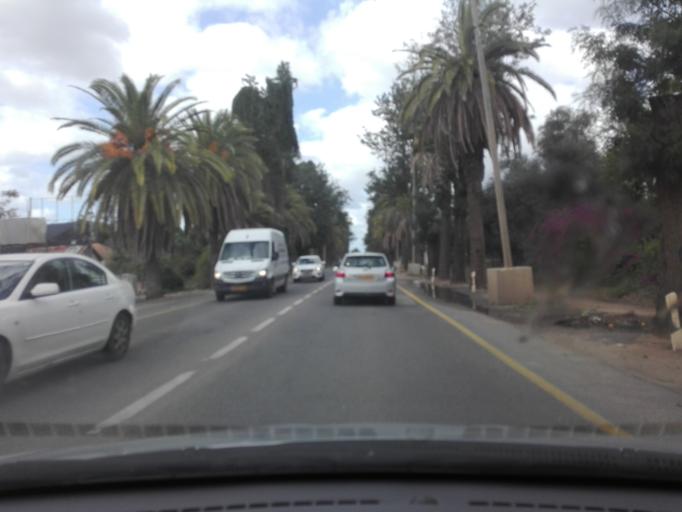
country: IL
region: Haifa
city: Hadera
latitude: 32.4782
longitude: 34.9751
